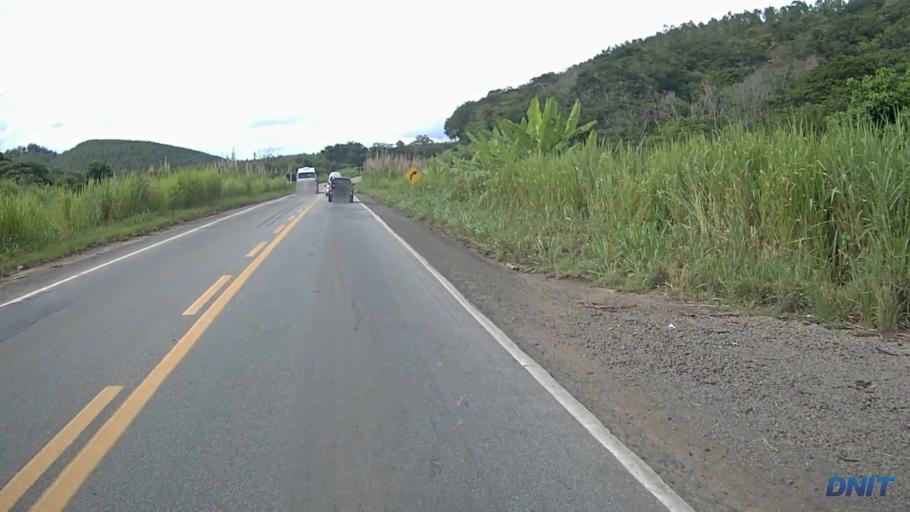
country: BR
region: Minas Gerais
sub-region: Ipaba
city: Ipaba
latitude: -19.3467
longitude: -42.4327
